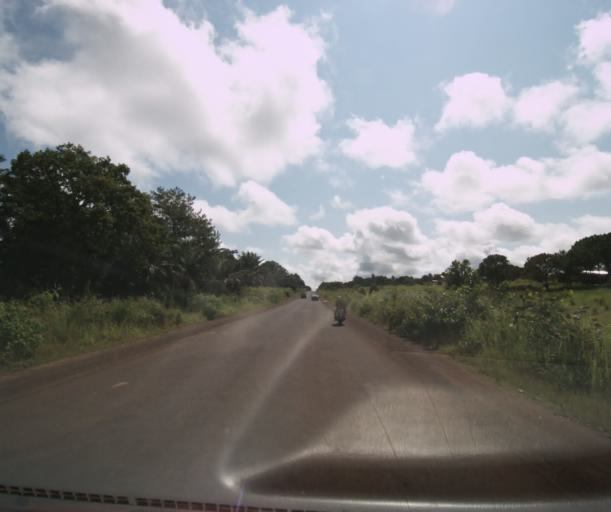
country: CM
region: West
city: Foumban
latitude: 5.6629
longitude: 10.7781
